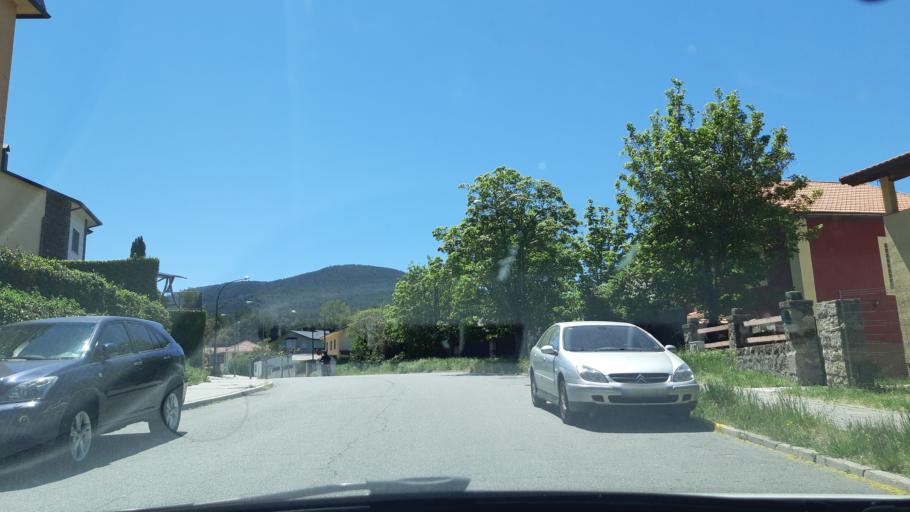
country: ES
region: Castille and Leon
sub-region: Provincia de Avila
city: Peguerinos
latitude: 40.7167
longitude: -4.1966
